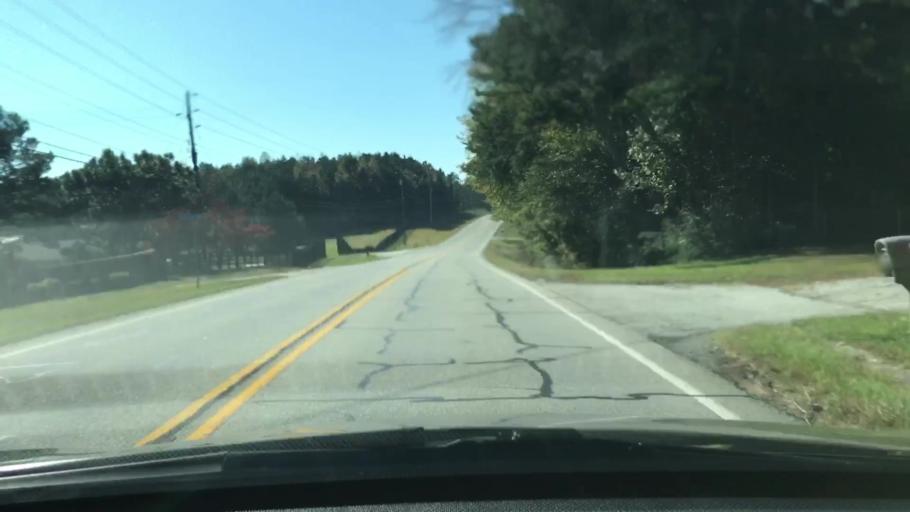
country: US
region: Georgia
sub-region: Carroll County
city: Villa Rica
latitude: 33.7950
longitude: -84.8936
